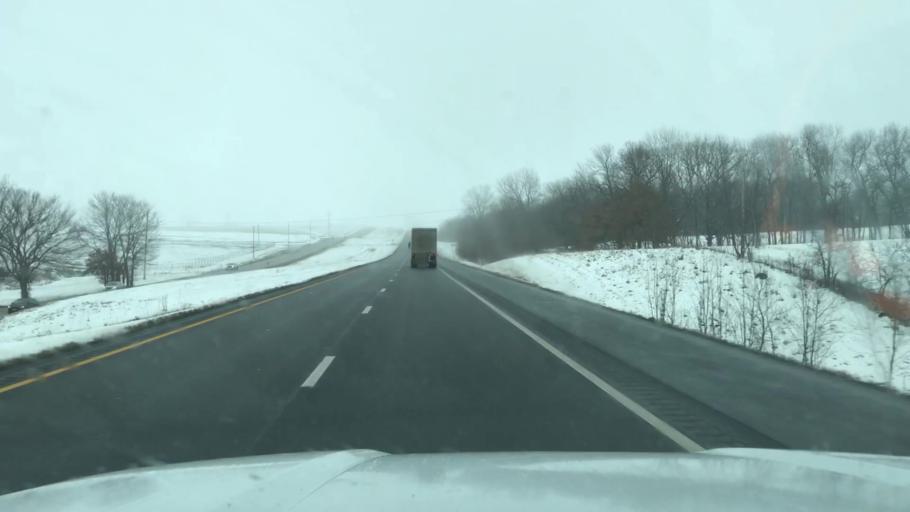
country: US
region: Missouri
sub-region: DeKalb County
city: Maysville
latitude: 39.7619
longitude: -94.4594
